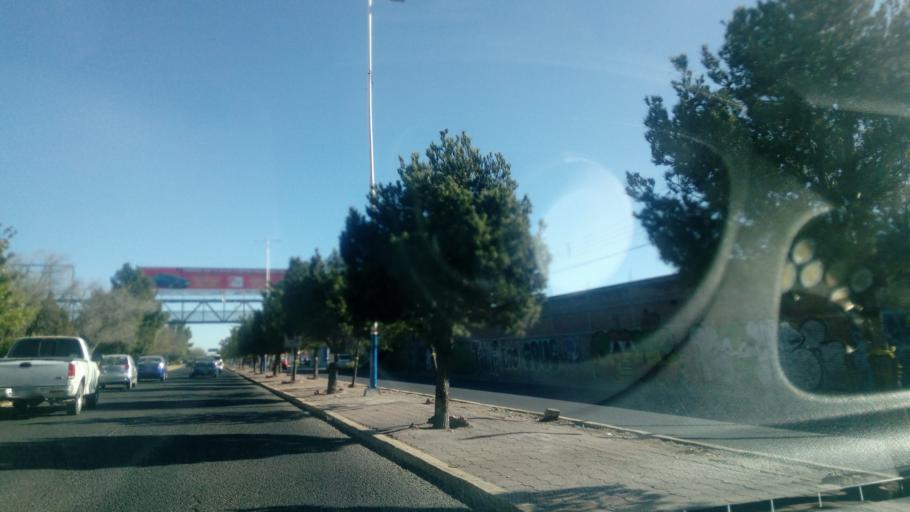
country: MX
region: Durango
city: Victoria de Durango
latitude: 24.0433
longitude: -104.6276
